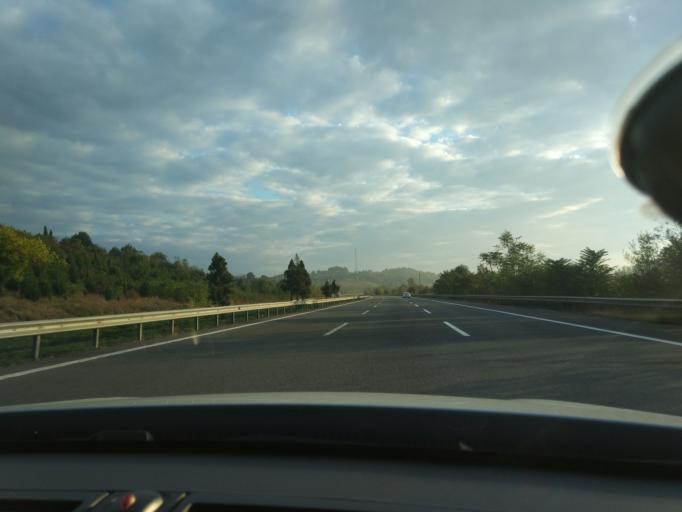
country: TR
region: Sakarya
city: Hendek
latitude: 40.7622
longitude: 30.7554
